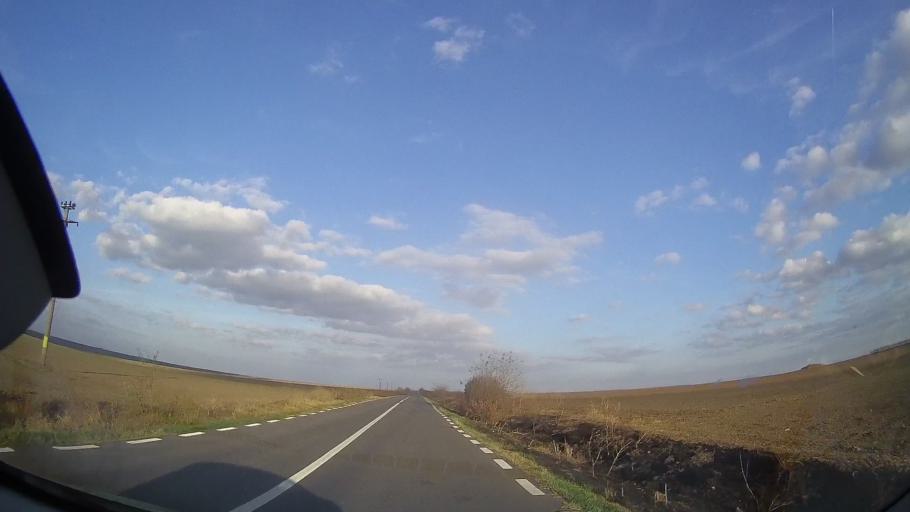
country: RO
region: Constanta
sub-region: Comuna Dumbraveni
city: Dumbraveni
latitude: 43.9340
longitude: 28.0250
